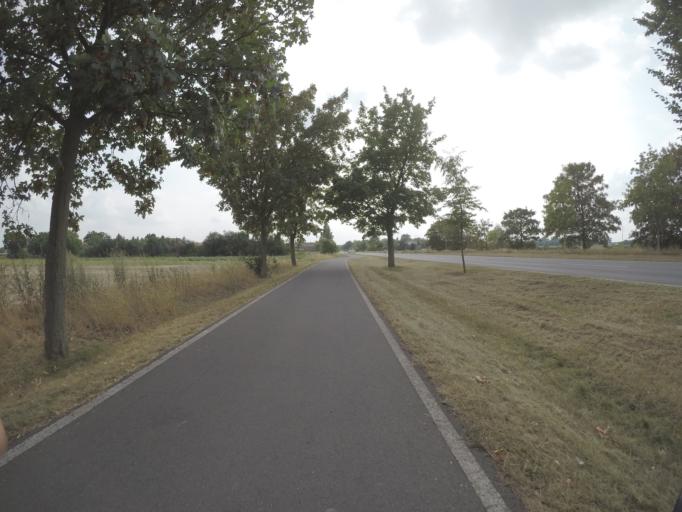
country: DE
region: Brandenburg
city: Schonefeld
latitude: 52.3735
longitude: 13.4794
